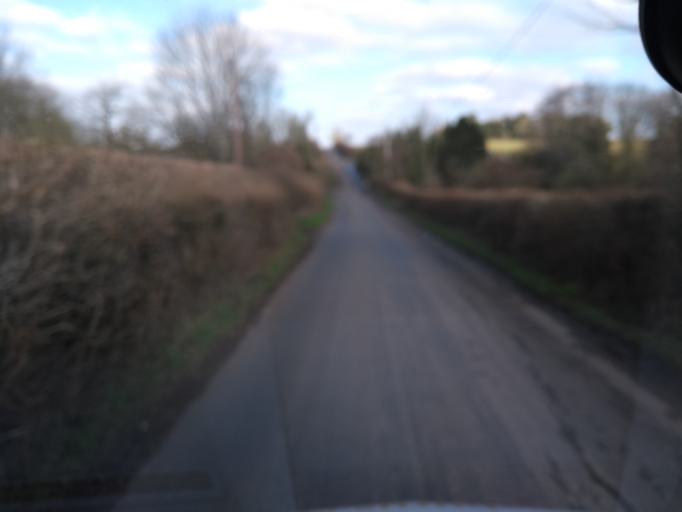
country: GB
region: England
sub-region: Somerset
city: Creech Saint Michael
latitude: 50.9605
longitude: -3.0242
